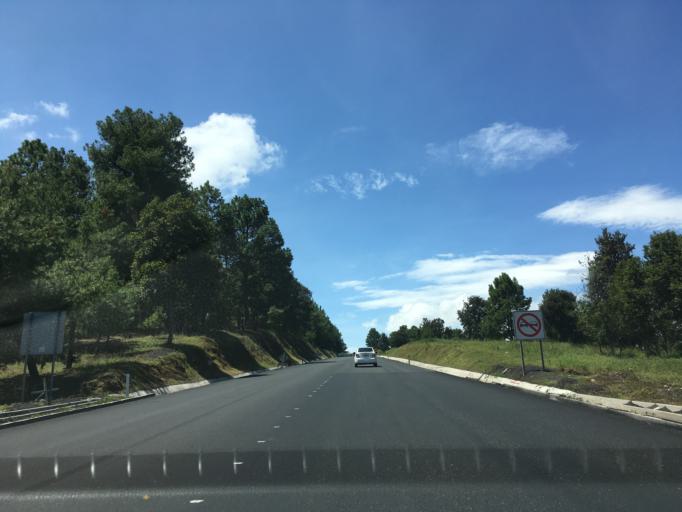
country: MX
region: Michoacan
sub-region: Patzcuaro
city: Santa Ana Chapitiro
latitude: 19.5004
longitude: -101.6953
